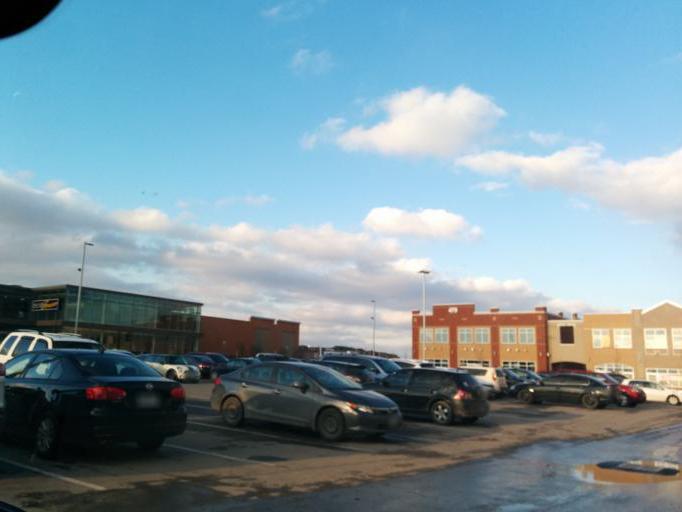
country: CA
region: Ontario
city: Oakville
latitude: 43.4660
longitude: -79.7447
